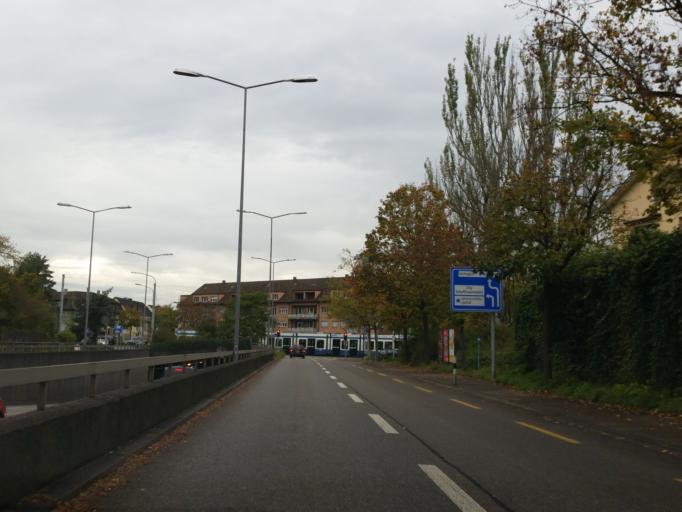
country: CH
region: Zurich
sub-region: Bezirk Zuerich
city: Zuerich (Kreis 6)
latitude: 47.3999
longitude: 8.5442
